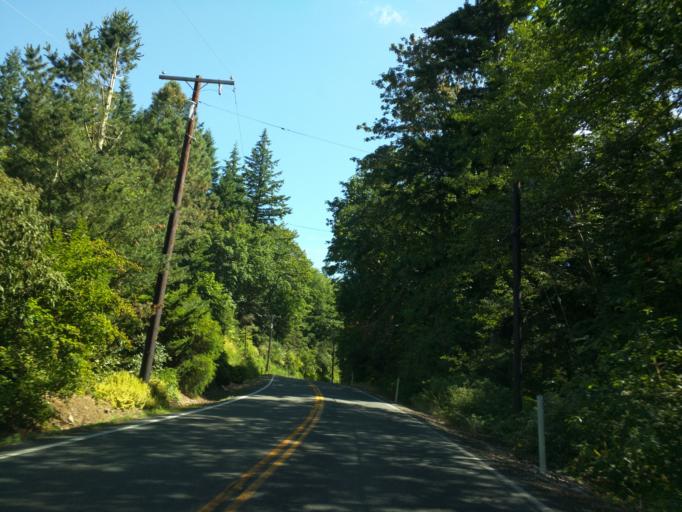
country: US
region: Washington
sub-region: Whatcom County
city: Sumas
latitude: 48.9697
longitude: -122.2080
